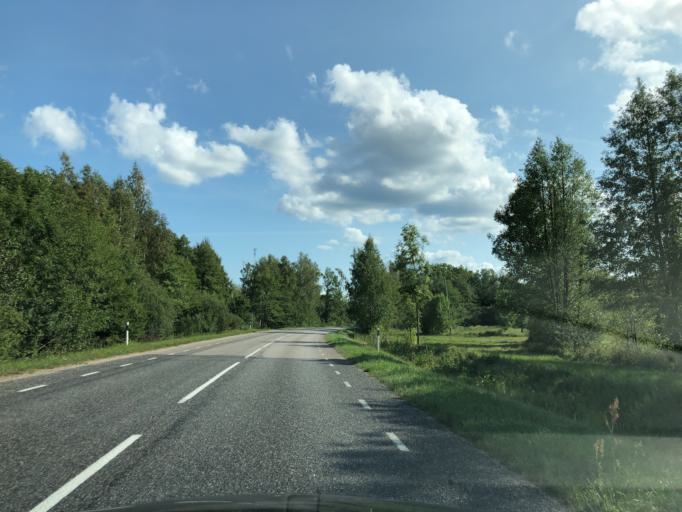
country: EE
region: Hiiumaa
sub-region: Kaerdla linn
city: Kardla
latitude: 58.7246
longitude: 22.5607
